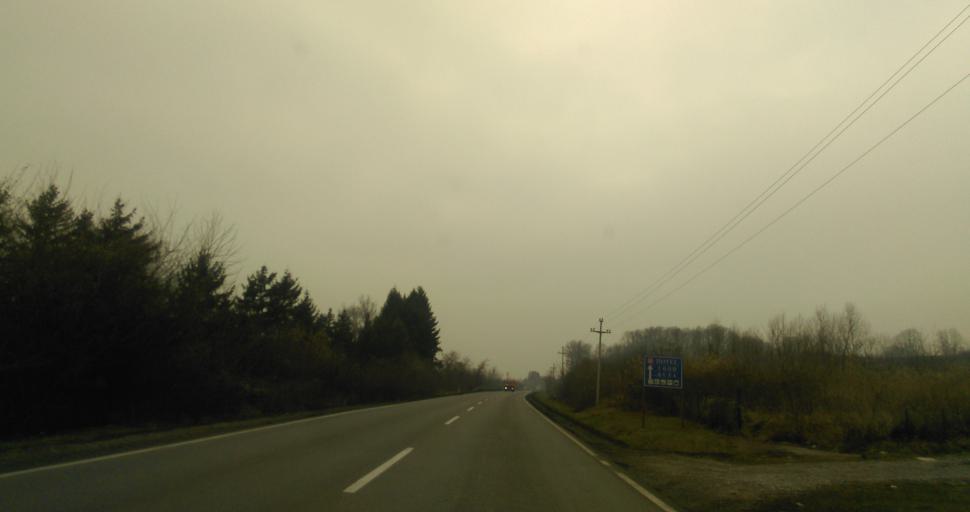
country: RS
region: Central Serbia
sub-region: Belgrade
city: Zvezdara
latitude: 44.7170
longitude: 20.5155
